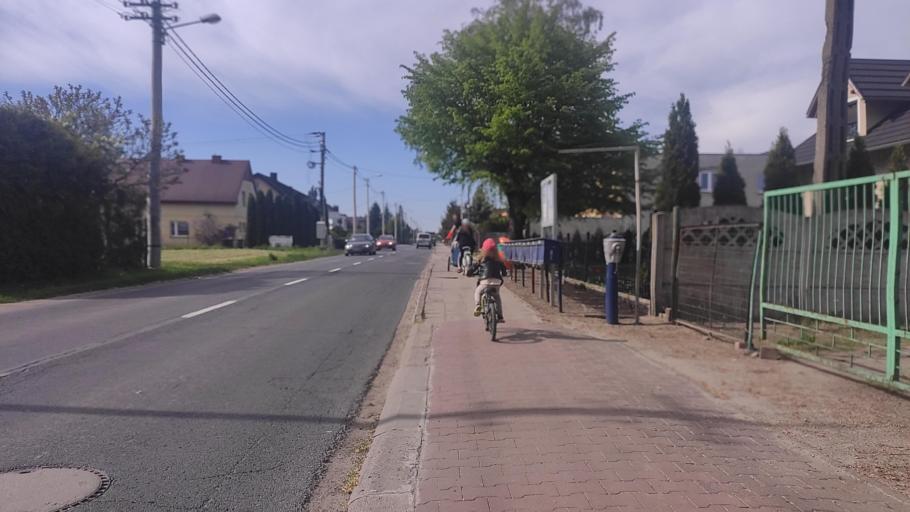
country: PL
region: Greater Poland Voivodeship
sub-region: Powiat poznanski
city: Kleszczewo
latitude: 52.3851
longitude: 17.1612
